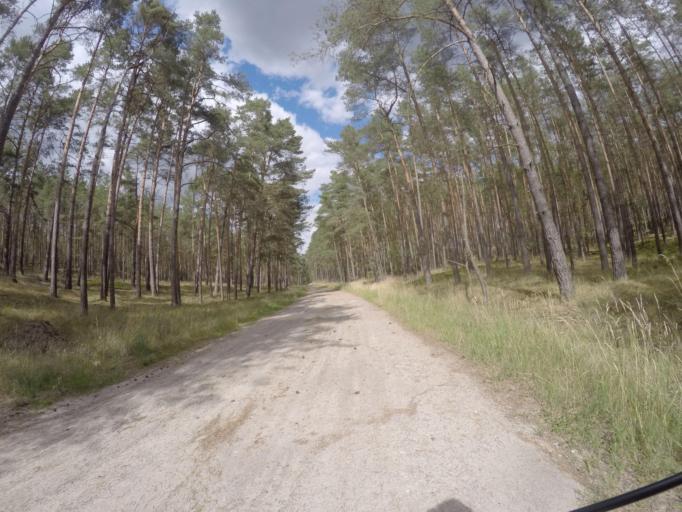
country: DE
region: Lower Saxony
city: Neu Darchau
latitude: 53.2604
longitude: 10.9773
